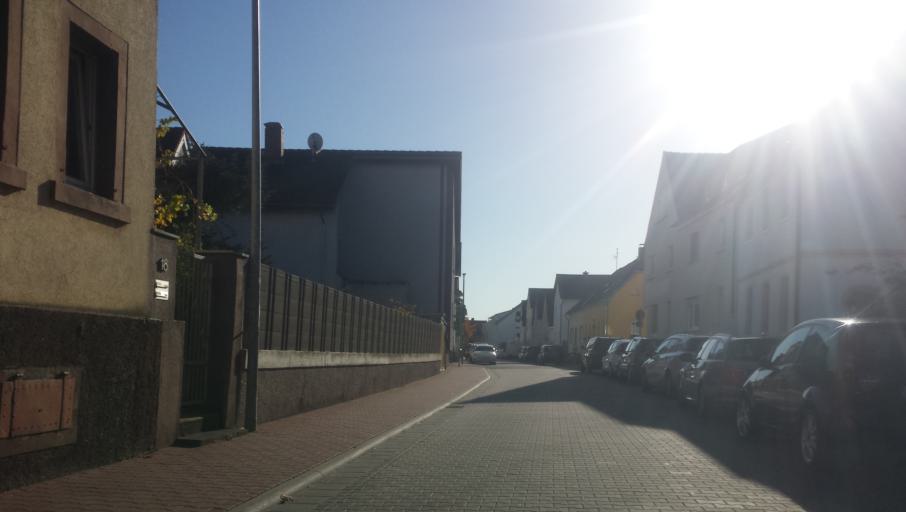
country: DE
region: Hesse
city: Gernsheim
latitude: 49.7503
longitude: 8.4860
